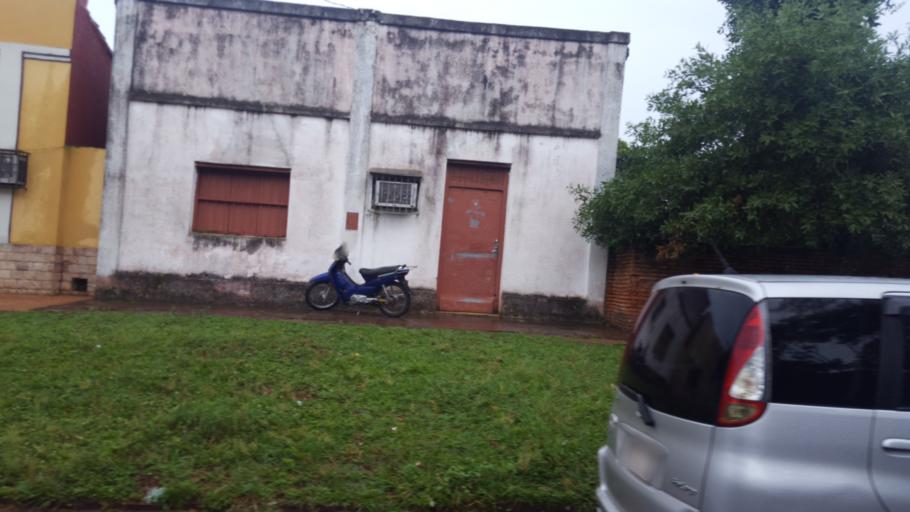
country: PY
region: Misiones
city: San Juan Bautista
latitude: -26.6699
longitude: -57.1495
